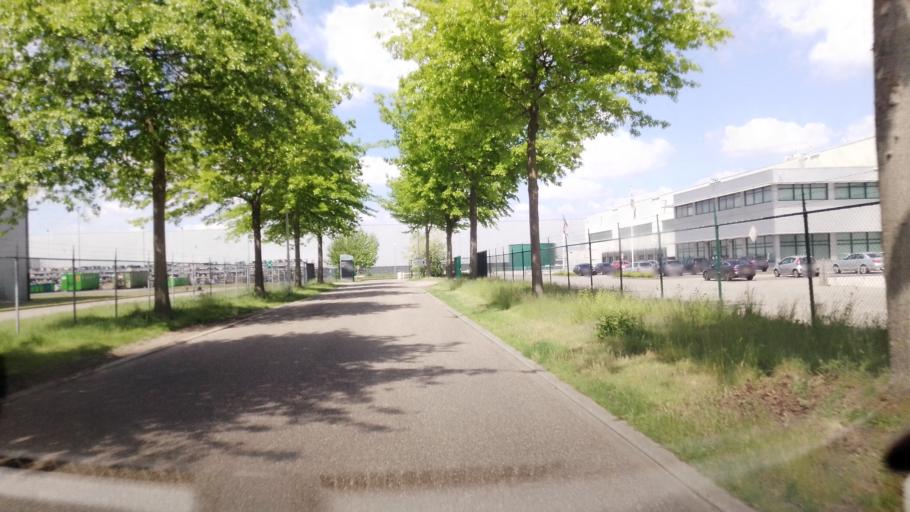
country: NL
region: Limburg
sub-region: Gemeente Peel en Maas
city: Maasbree
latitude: 51.4029
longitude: 6.0751
